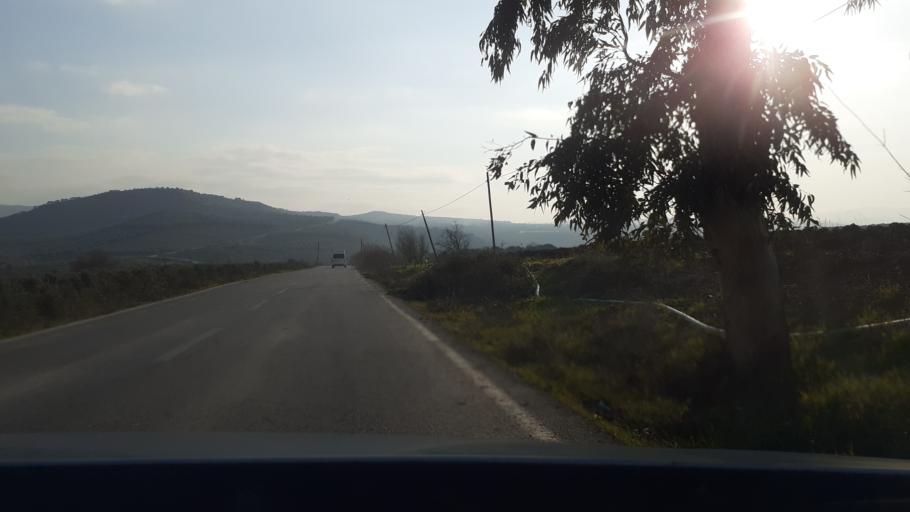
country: TR
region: Hatay
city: Oymakli
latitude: 36.1318
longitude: 36.3109
